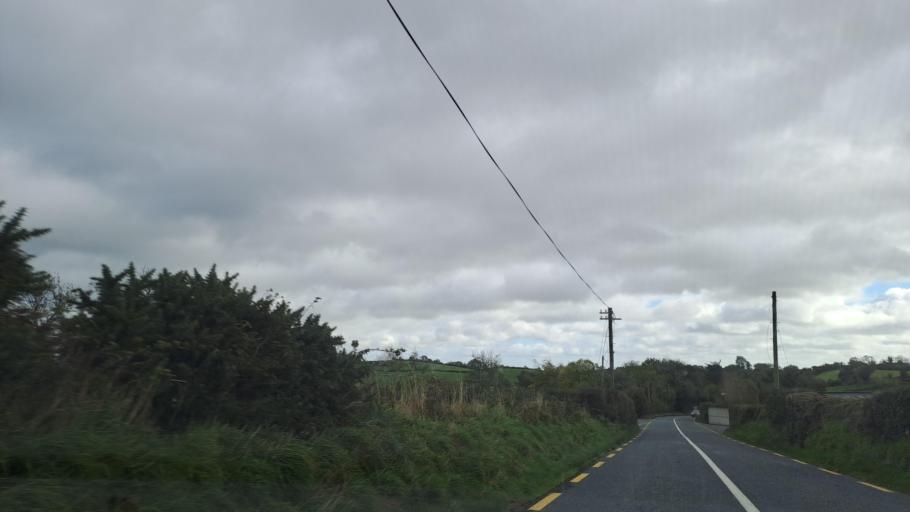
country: IE
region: Ulster
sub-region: An Cabhan
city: Kingscourt
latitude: 53.9180
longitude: -6.8594
